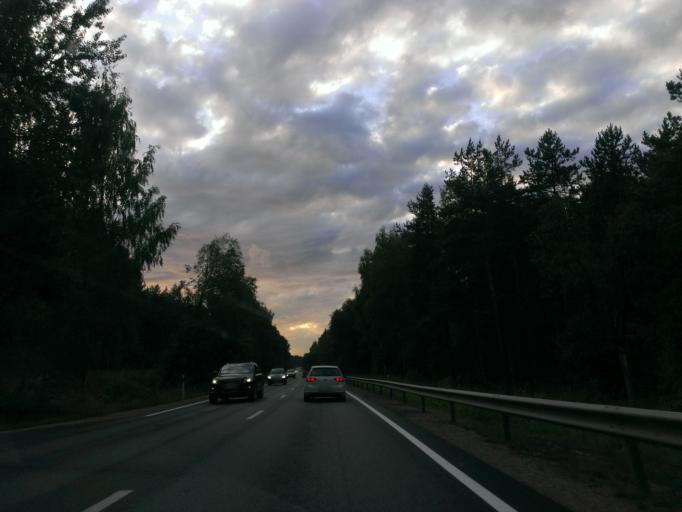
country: LV
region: Riga
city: Bergi
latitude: 56.9653
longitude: 24.3663
